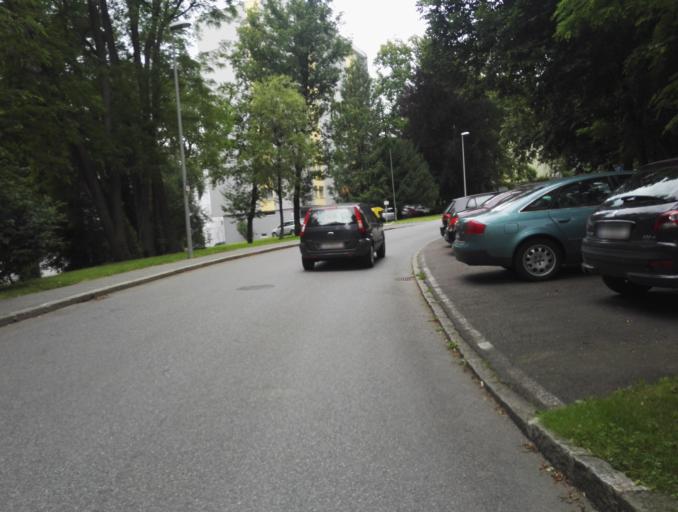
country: AT
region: Styria
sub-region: Graz Stadt
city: Graz
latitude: 47.0799
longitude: 15.4716
